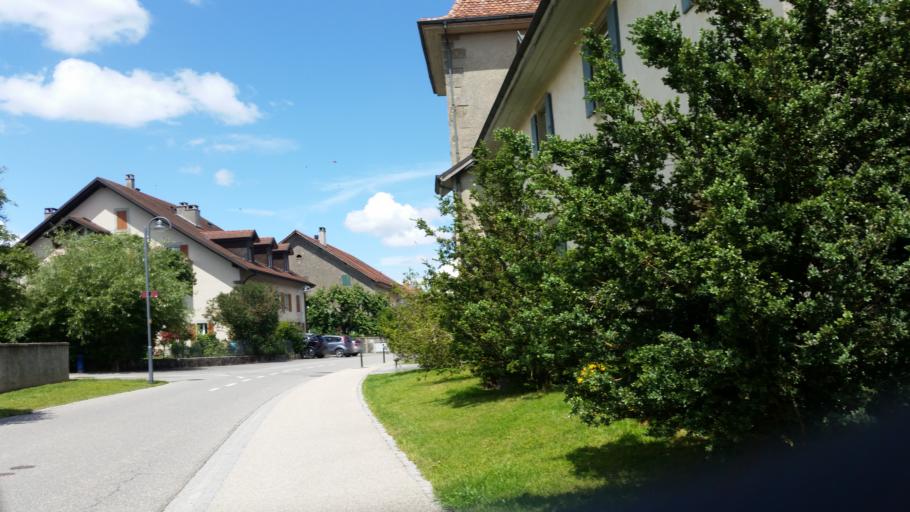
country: CH
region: Vaud
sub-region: Gros-de-Vaud District
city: Penthereaz
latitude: 46.6568
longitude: 6.6043
